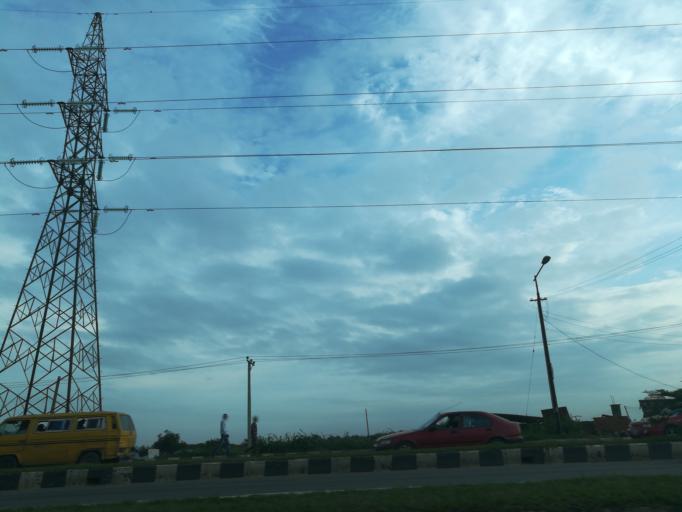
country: NG
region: Lagos
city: Ebute Ikorodu
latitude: 6.6188
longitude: 3.4675
